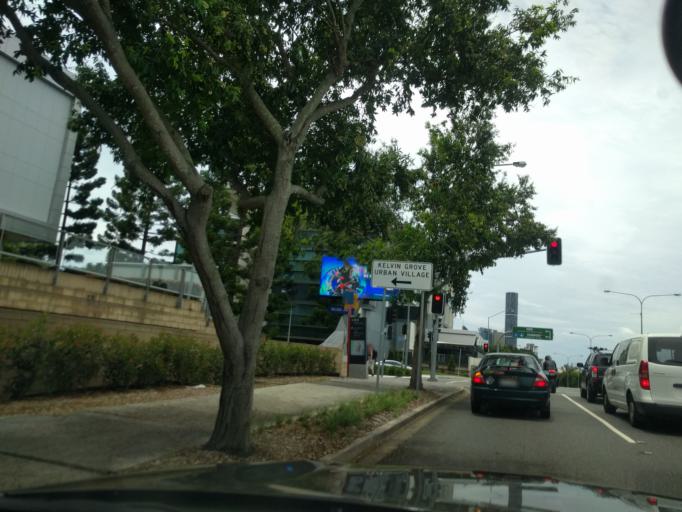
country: AU
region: Queensland
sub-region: Brisbane
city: Spring Hill
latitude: -27.4554
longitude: 153.0127
